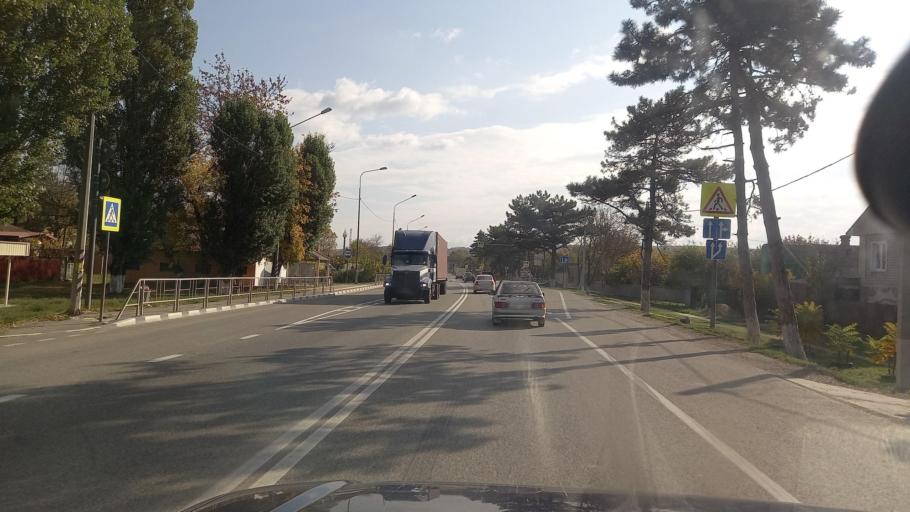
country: RU
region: Krasnodarskiy
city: Krymsk
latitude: 44.8685
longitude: 37.8610
